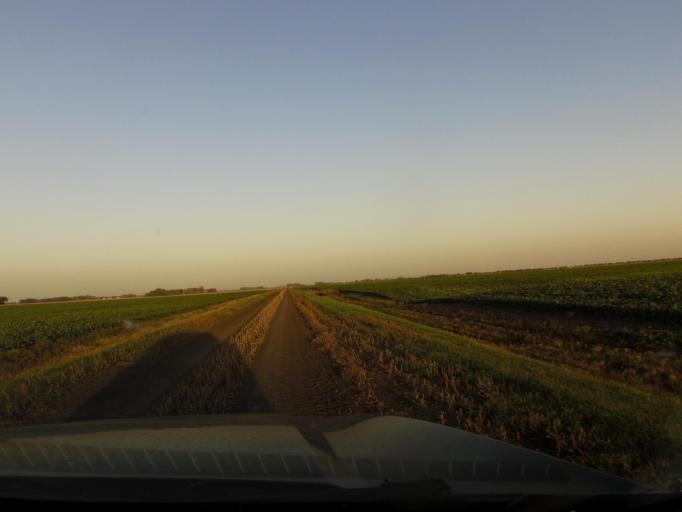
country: US
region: North Dakota
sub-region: Walsh County
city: Grafton
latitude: 48.3833
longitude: -97.2416
